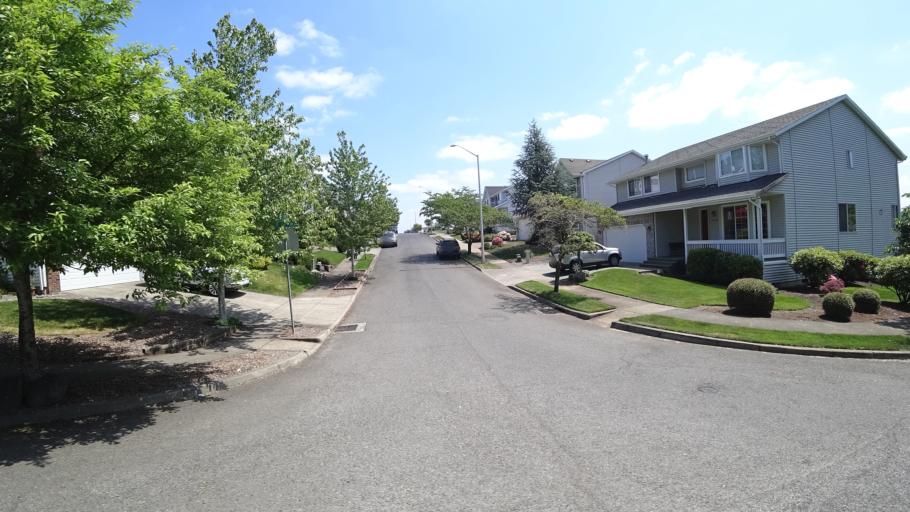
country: US
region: Oregon
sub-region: Clackamas County
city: Happy Valley
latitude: 45.4710
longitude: -122.5069
